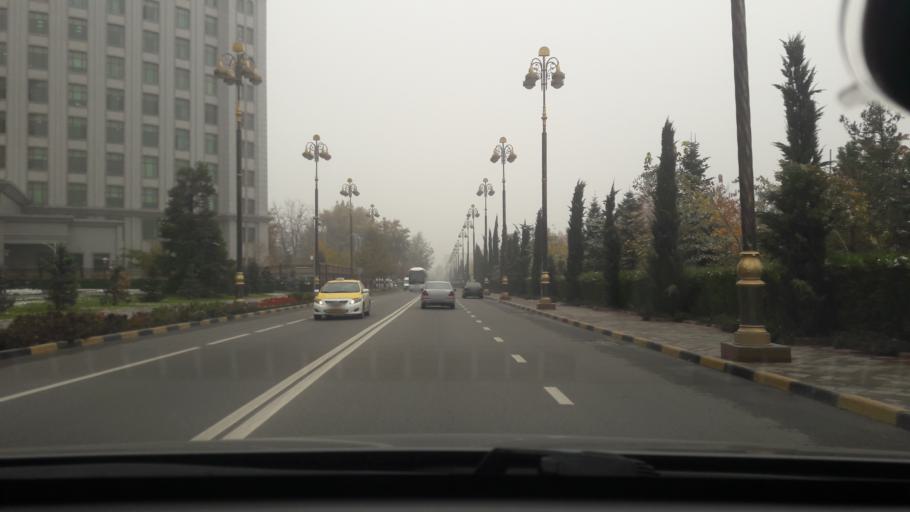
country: TJ
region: Dushanbe
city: Dushanbe
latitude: 38.5797
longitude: 68.7822
